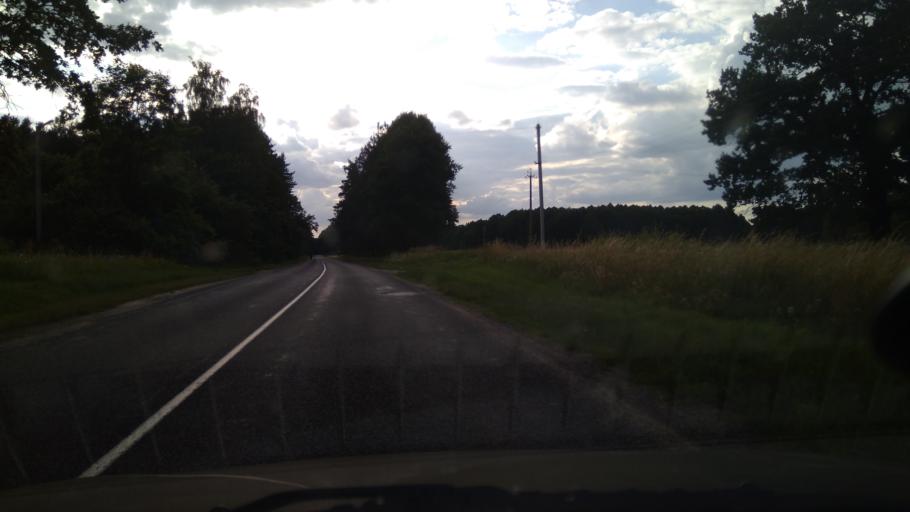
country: BY
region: Grodnenskaya
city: Masty
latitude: 53.3452
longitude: 24.6657
